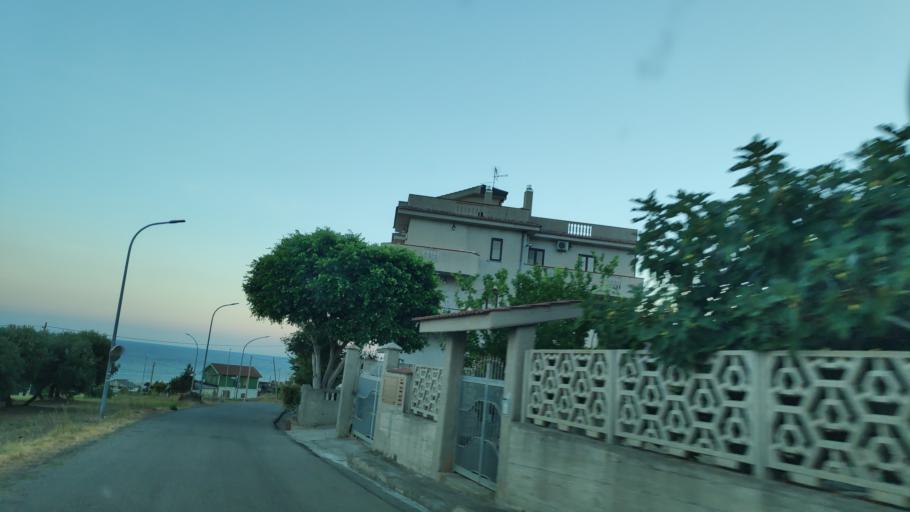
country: IT
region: Calabria
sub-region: Provincia di Reggio Calabria
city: Riace Marina
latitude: 38.3928
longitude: 16.5284
